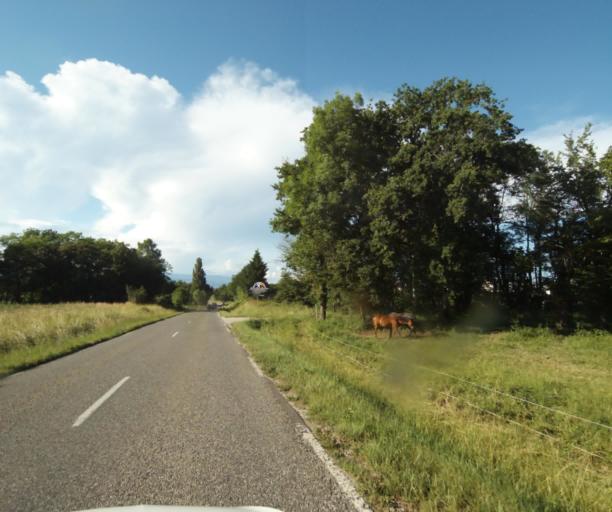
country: FR
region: Rhone-Alpes
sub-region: Departement de la Haute-Savoie
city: Messery
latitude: 46.3415
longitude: 6.2919
